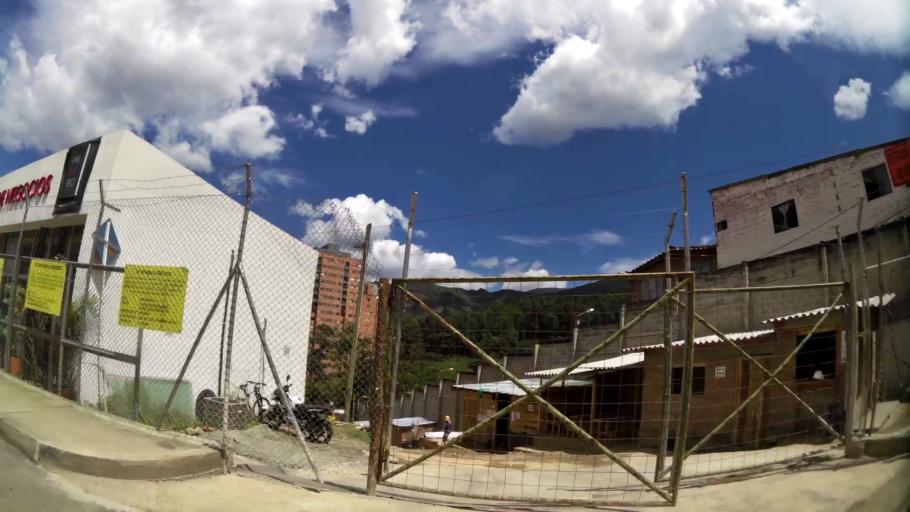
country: CO
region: Antioquia
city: Sabaneta
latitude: 6.1411
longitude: -75.6215
